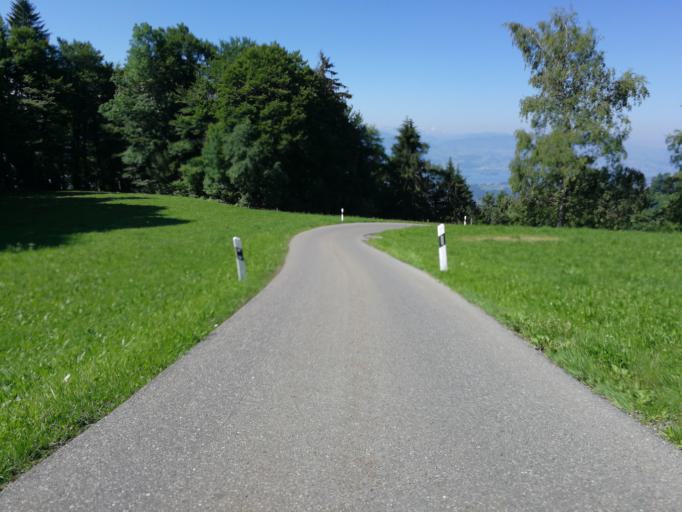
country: CH
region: Zurich
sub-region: Bezirk Hinwil
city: Wald
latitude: 47.2897
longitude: 8.8879
